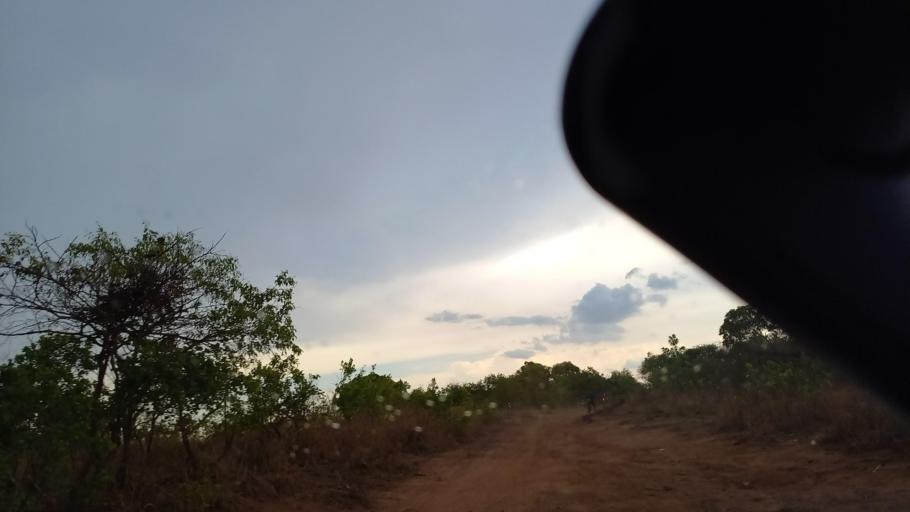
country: ZM
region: Lusaka
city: Kafue
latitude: -15.9886
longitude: 28.2690
